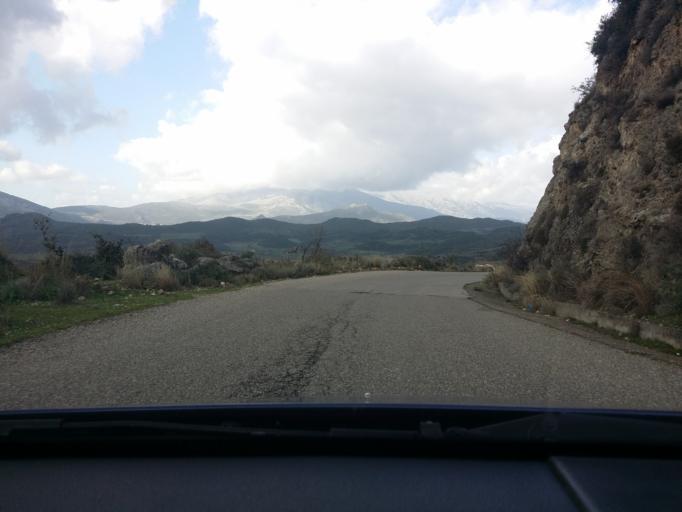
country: GR
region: West Greece
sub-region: Nomos Aitolias kai Akarnanias
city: Fitiai
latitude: 38.6926
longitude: 21.1786
